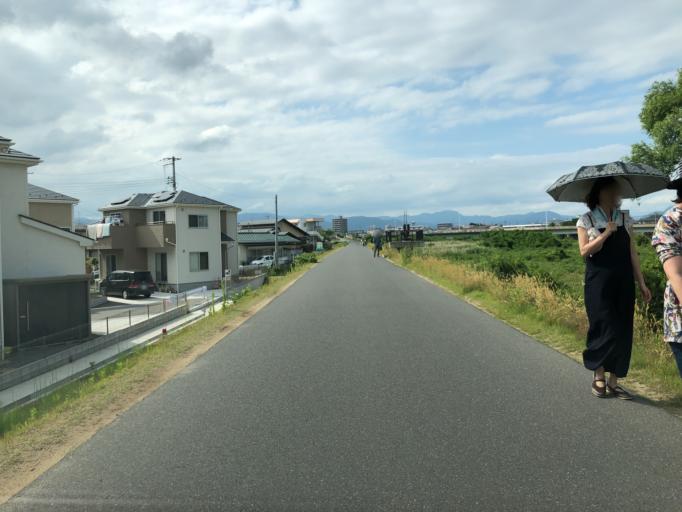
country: JP
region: Fukushima
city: Fukushima-shi
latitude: 37.7491
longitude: 140.4524
